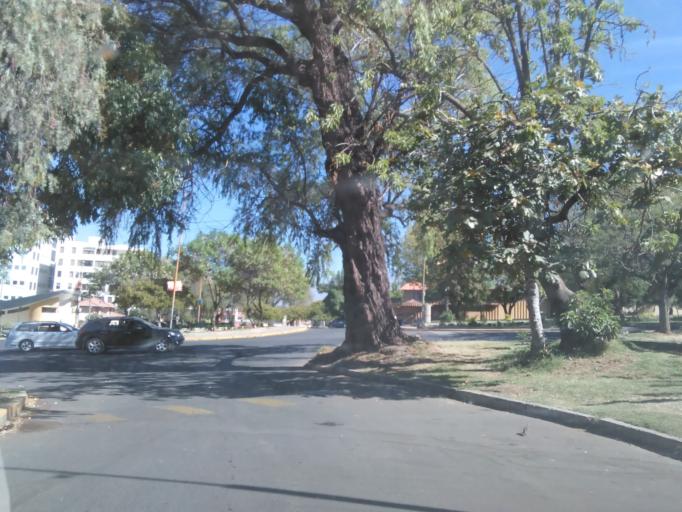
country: BO
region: Cochabamba
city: Cochabamba
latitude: -17.3689
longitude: -66.1584
